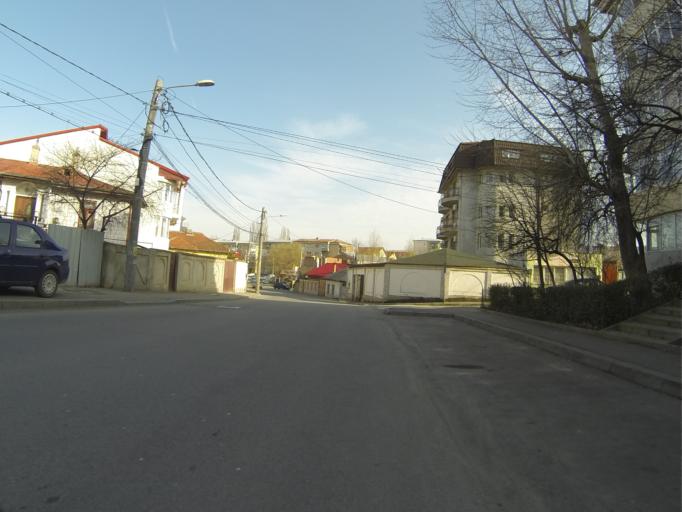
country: RO
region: Dolj
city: Craiova
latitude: 44.3080
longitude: 23.8132
